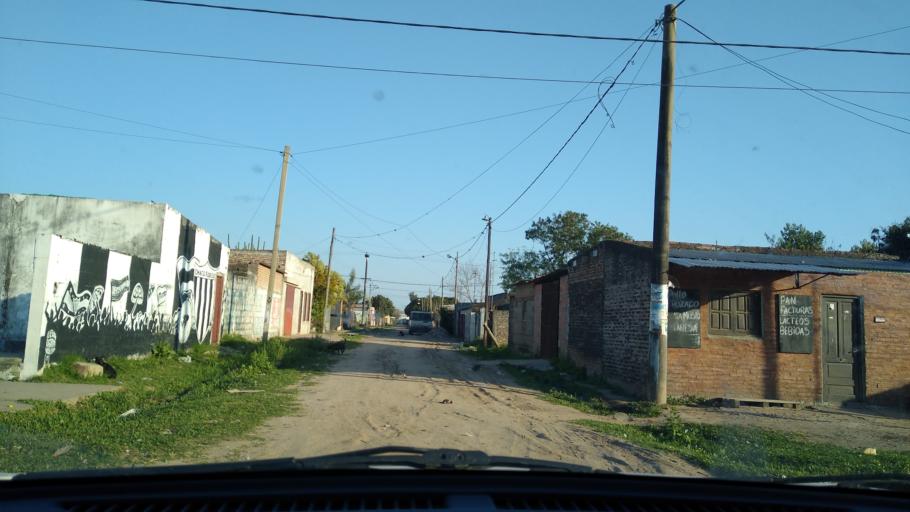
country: AR
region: Chaco
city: Resistencia
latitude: -27.4837
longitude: -58.9703
